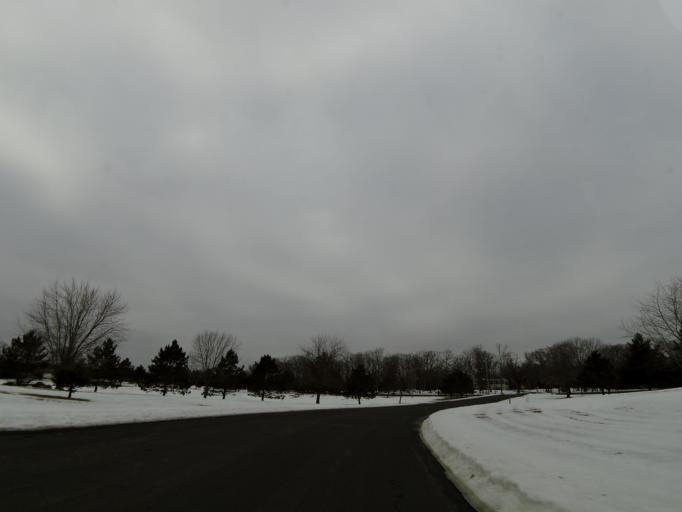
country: US
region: Minnesota
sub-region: Washington County
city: Afton
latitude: 44.8495
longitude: -92.7955
